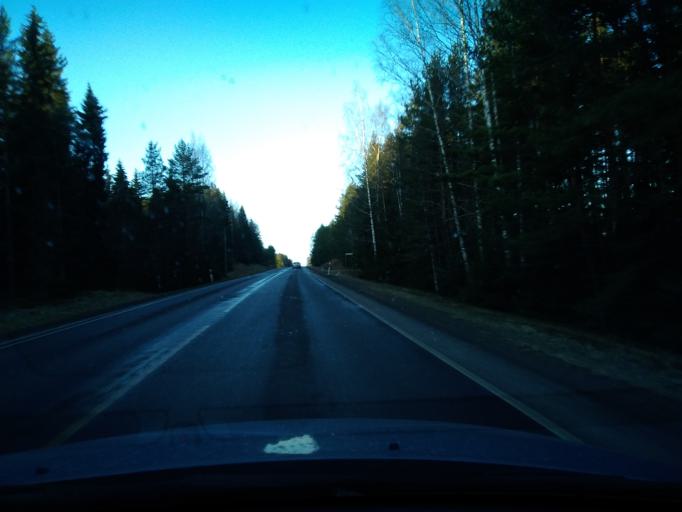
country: FI
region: Haeme
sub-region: Riihimaeki
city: Loppi
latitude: 60.7230
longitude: 24.4296
